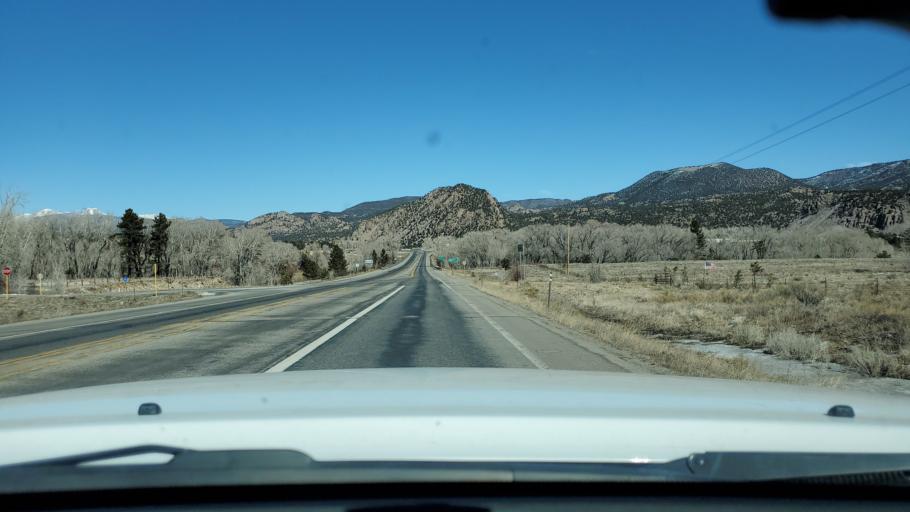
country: US
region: Colorado
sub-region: Chaffee County
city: Buena Vista
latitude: 38.7382
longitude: -106.0849
